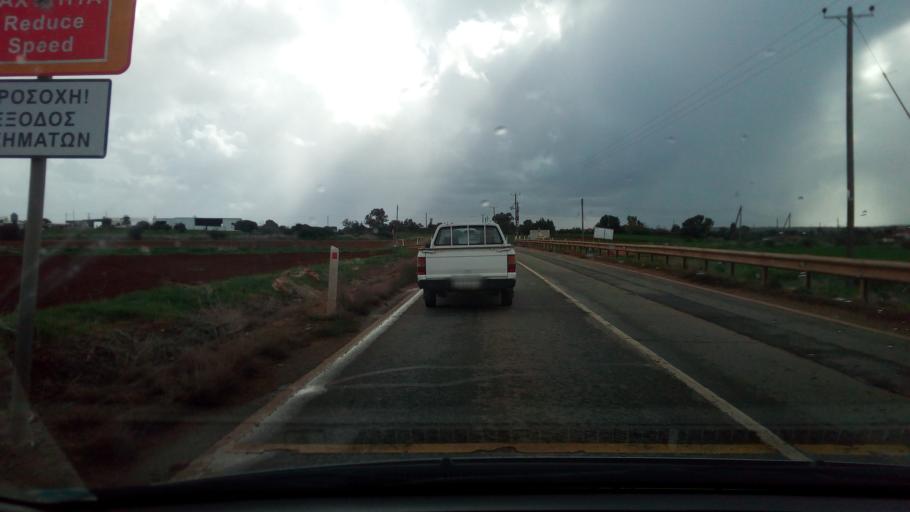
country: CY
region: Ammochostos
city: Liopetri
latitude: 34.9967
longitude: 33.8921
